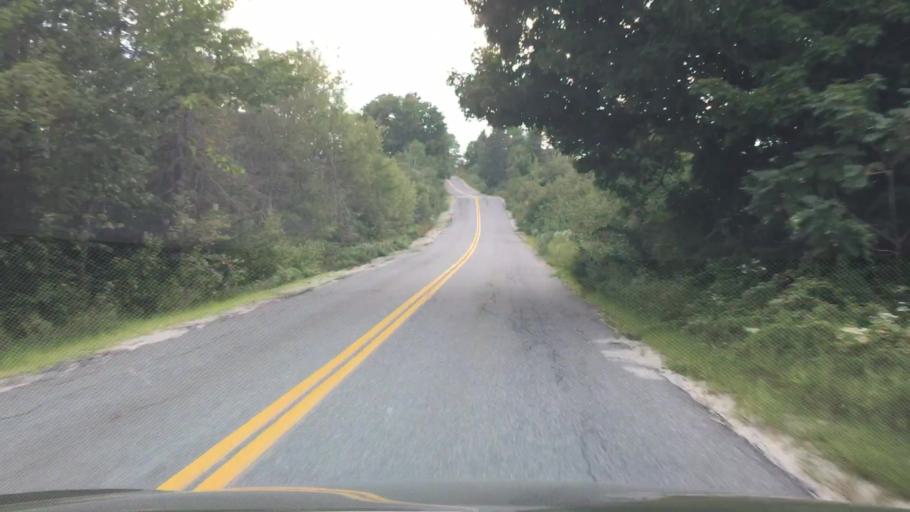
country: US
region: Maine
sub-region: Hancock County
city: Penobscot
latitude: 44.4439
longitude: -68.6333
